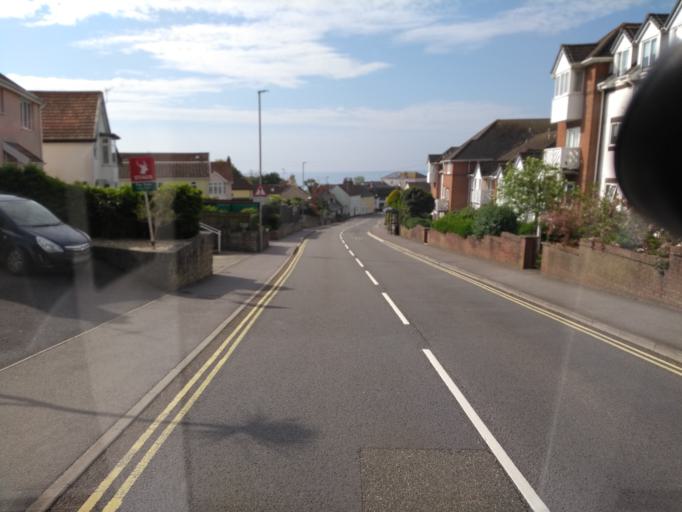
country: GB
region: England
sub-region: Dorset
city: Lyme Regis
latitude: 50.7280
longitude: -2.9314
